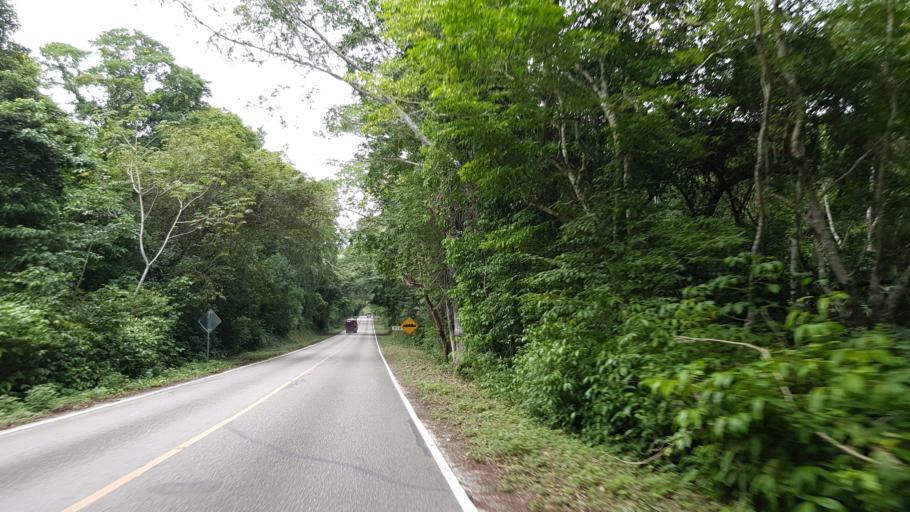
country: GT
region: Peten
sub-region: Municipio de San Jose
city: San Jose
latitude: 17.2189
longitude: -89.6116
